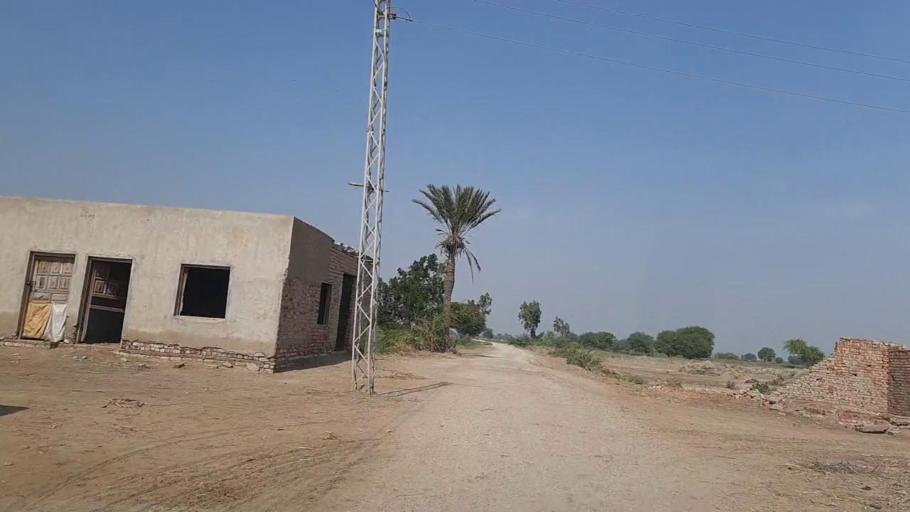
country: PK
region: Sindh
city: Samaro
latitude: 25.2555
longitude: 69.3946
